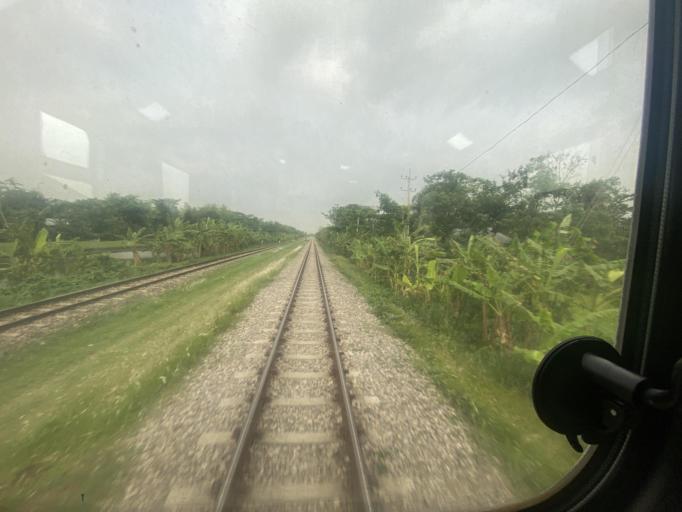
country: BD
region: Dhaka
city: Tungi
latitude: 23.9310
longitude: 90.5324
